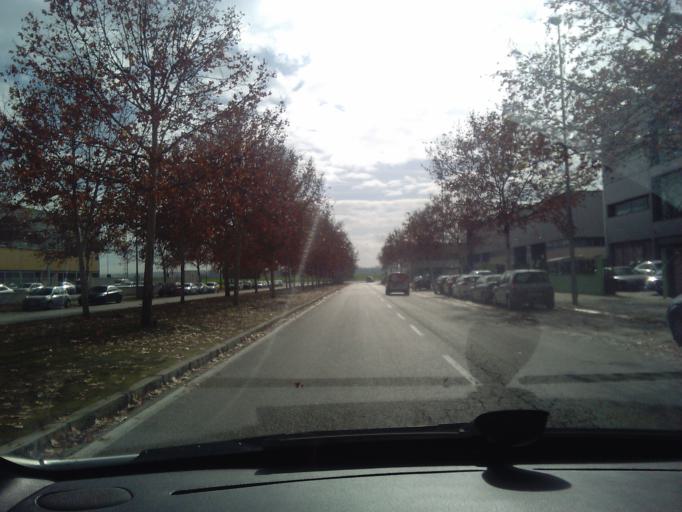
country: ES
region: Andalusia
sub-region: Provincia de Sevilla
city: Sevilla
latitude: 37.3758
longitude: -5.9194
